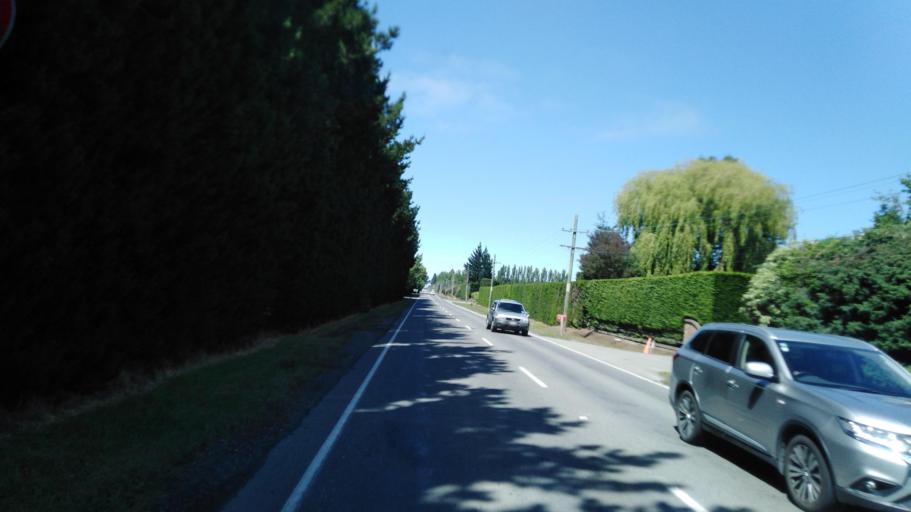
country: NZ
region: Canterbury
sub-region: Selwyn District
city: Prebbleton
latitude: -43.5154
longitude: 172.5073
